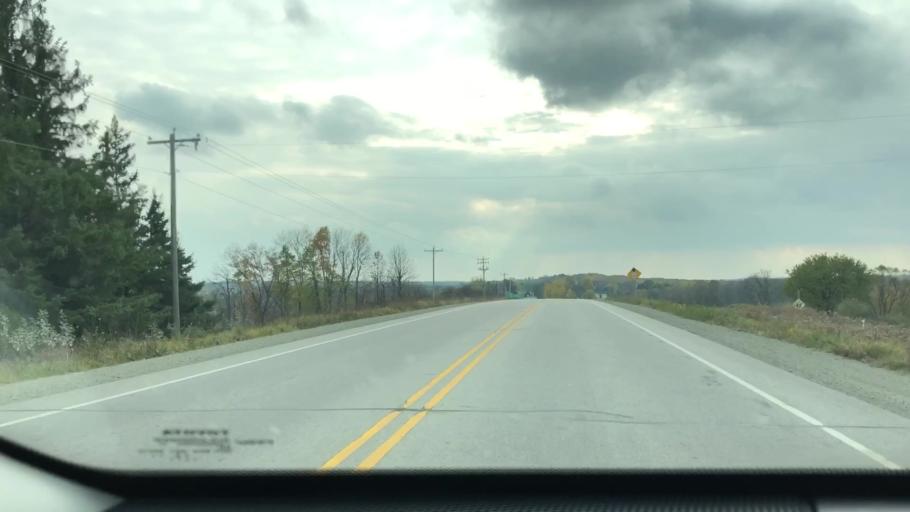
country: US
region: Wisconsin
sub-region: Brown County
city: Oneida
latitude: 44.5050
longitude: -88.1725
